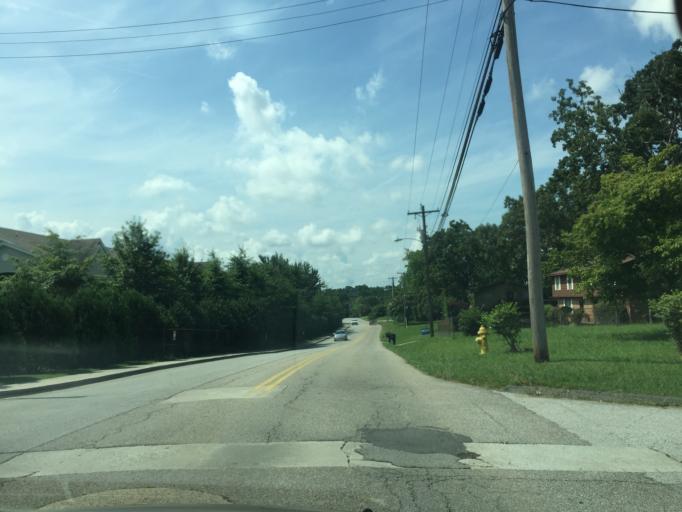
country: US
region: Tennessee
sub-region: Hamilton County
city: Harrison
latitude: 35.0922
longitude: -85.1905
